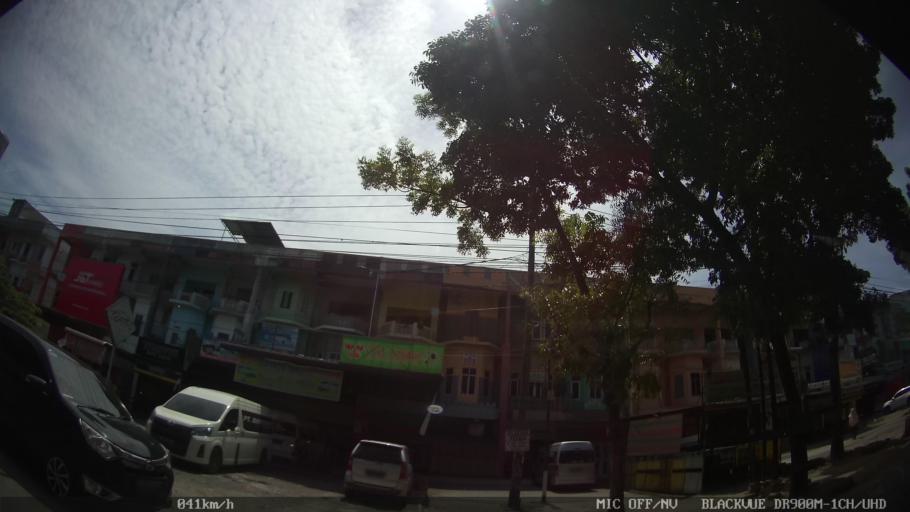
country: ID
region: North Sumatra
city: Sunggal
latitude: 3.5804
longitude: 98.6268
